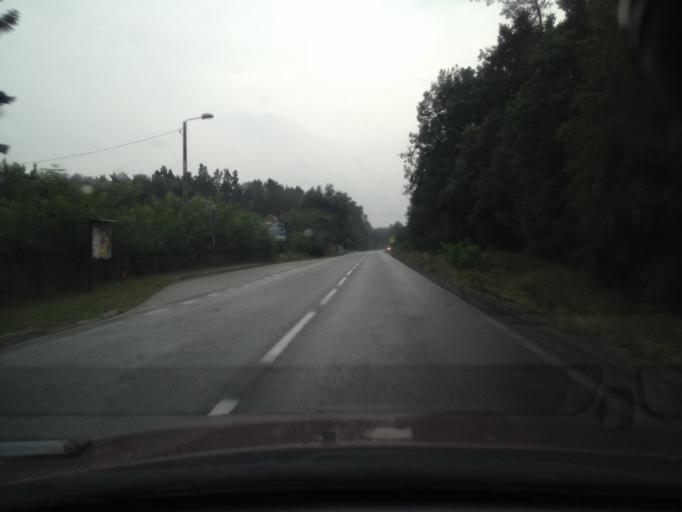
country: PL
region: Lubusz
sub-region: Powiat zaganski
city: Zagan
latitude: 51.5744
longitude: 15.2713
